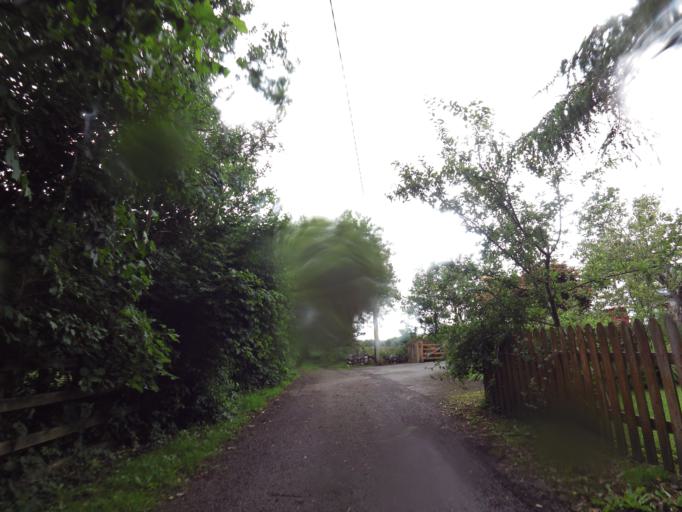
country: IE
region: Connaught
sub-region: County Galway
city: Athenry
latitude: 53.2852
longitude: -8.7041
